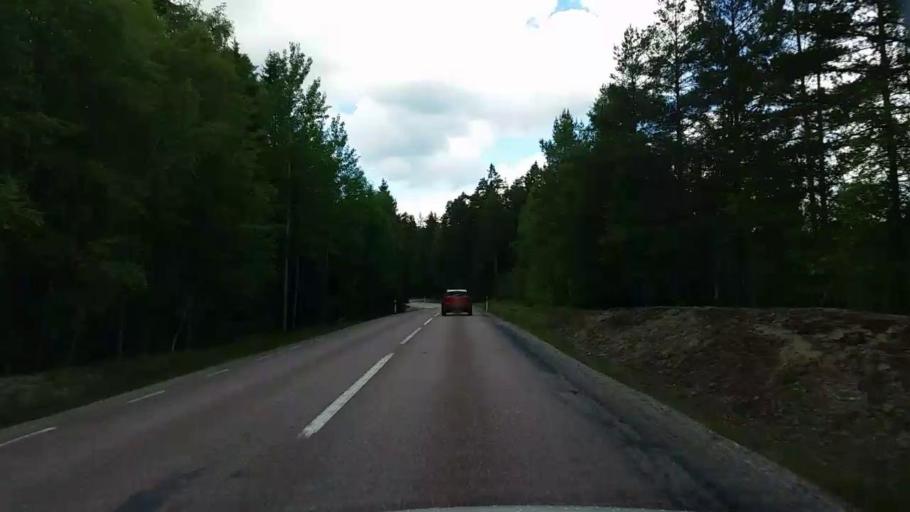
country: SE
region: Vaestmanland
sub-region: Fagersta Kommun
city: Fagersta
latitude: 59.8846
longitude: 15.8323
